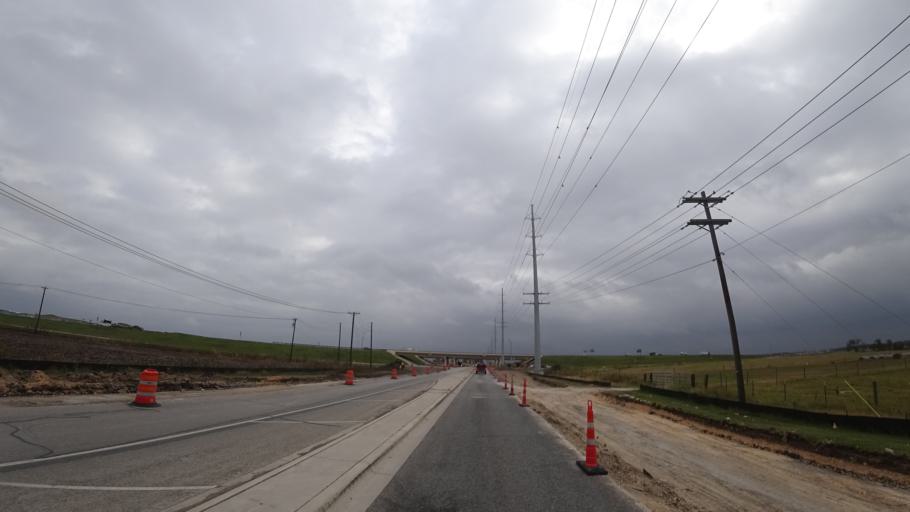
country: US
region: Texas
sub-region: Travis County
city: Pflugerville
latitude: 30.4531
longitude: -97.5967
